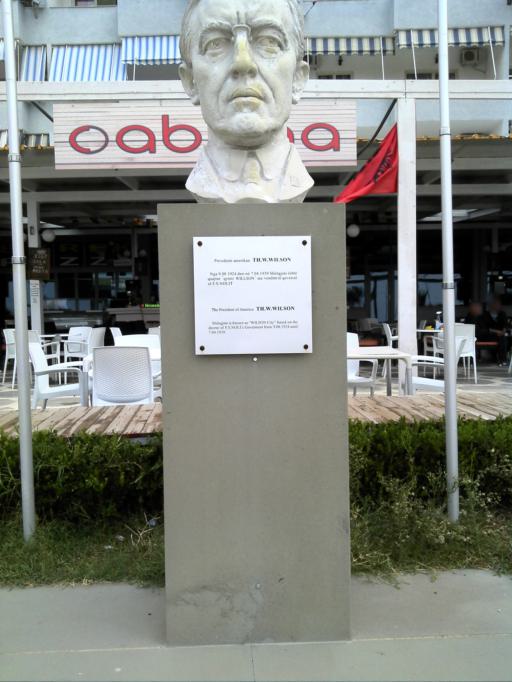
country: AL
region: Lezhe
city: Shengjin
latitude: 41.8094
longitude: 19.5973
